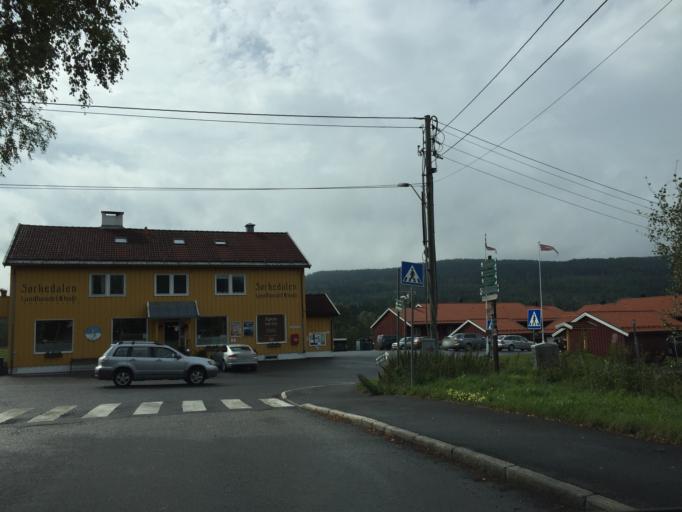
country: NO
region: Akershus
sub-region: Baerum
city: Lysaker
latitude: 60.0172
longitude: 10.6126
